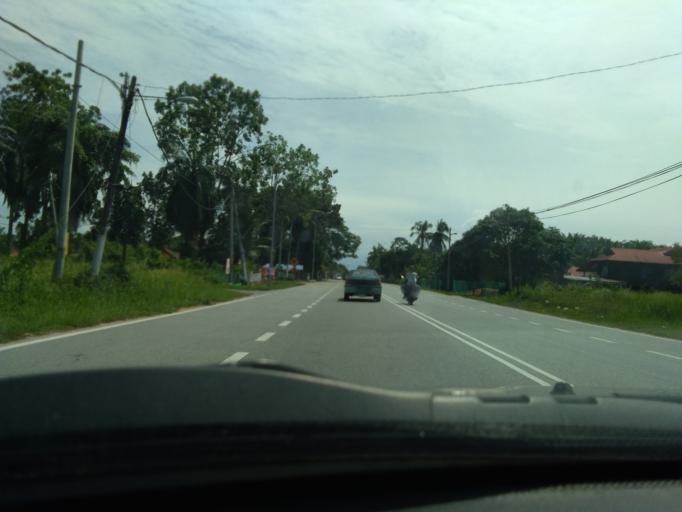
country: MY
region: Perak
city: Bagan Serai
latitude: 5.0317
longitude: 100.5618
